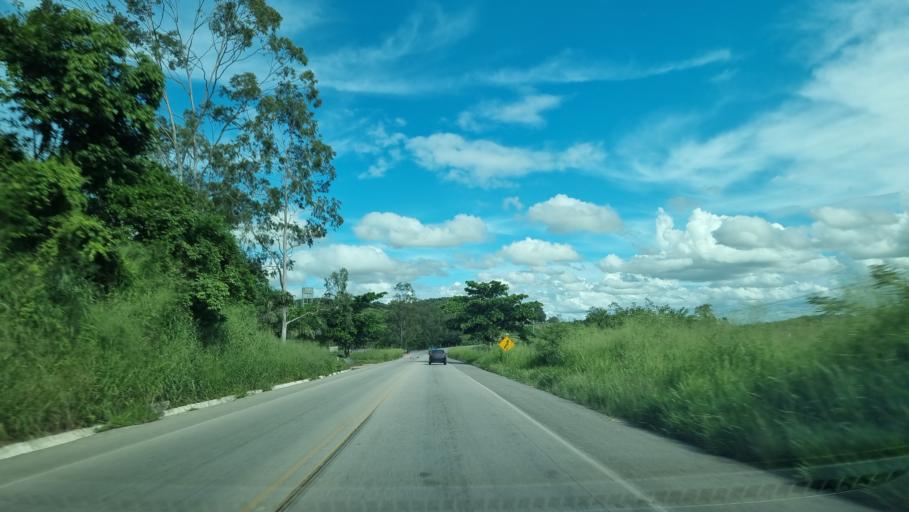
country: BR
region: Pernambuco
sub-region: Caruaru
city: Caruaru
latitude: -8.3694
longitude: -35.9844
